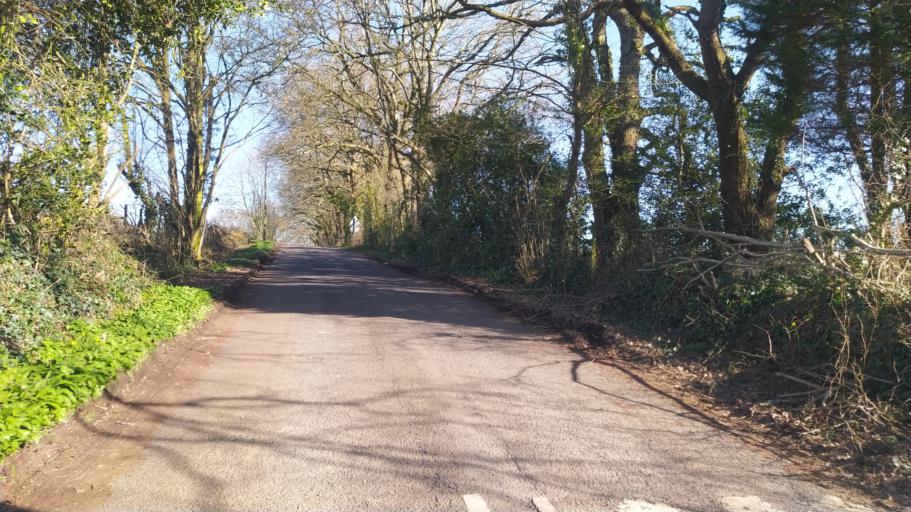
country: GB
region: England
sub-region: Dorset
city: Verwood
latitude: 50.8958
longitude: -1.8916
